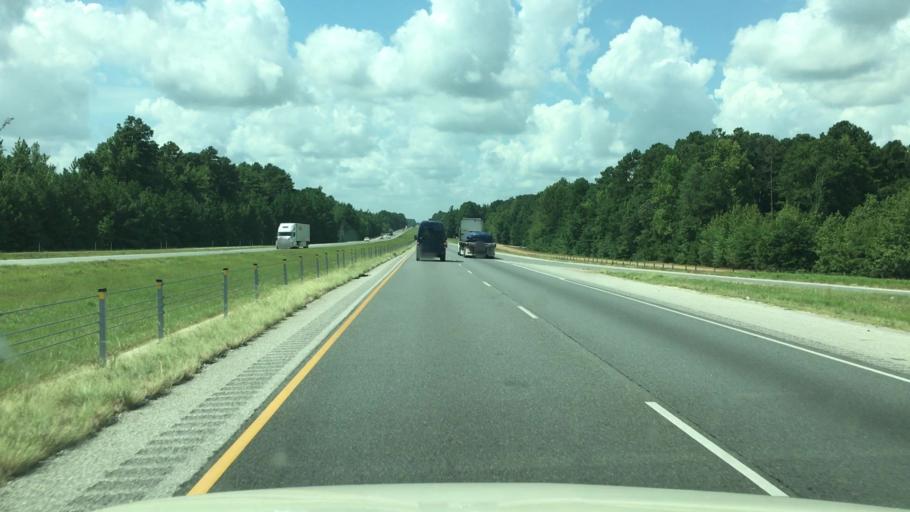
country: US
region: Arkansas
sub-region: Clark County
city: Arkadelphia
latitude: 34.0721
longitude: -93.1210
